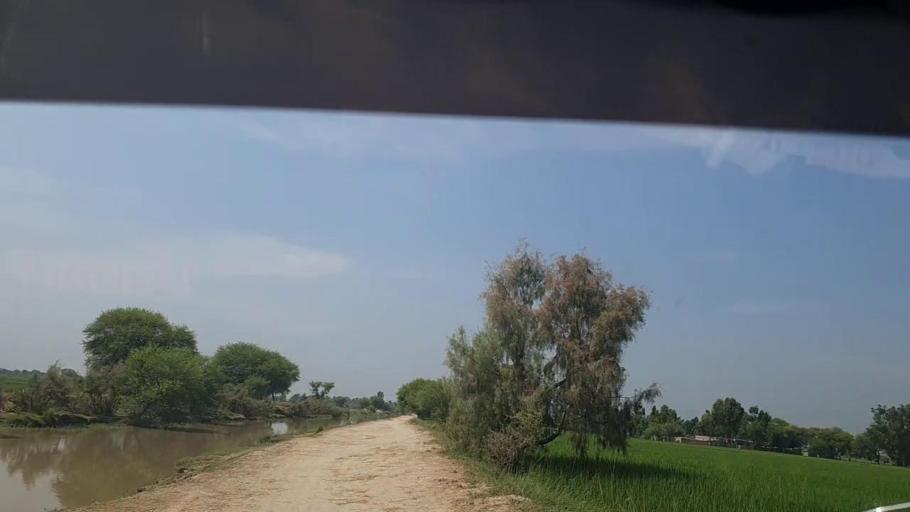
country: PK
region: Sindh
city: Thul
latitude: 28.1998
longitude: 68.7016
